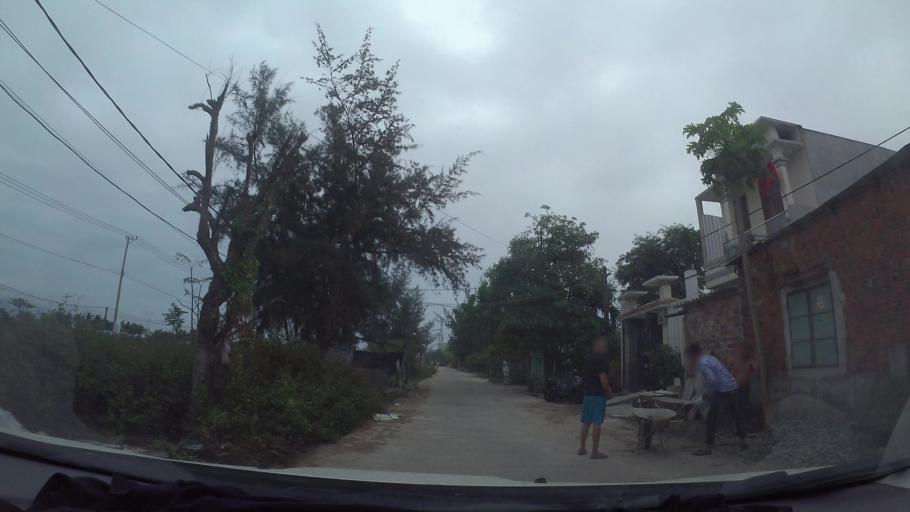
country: VN
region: Da Nang
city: Lien Chieu
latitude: 16.0865
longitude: 108.1560
